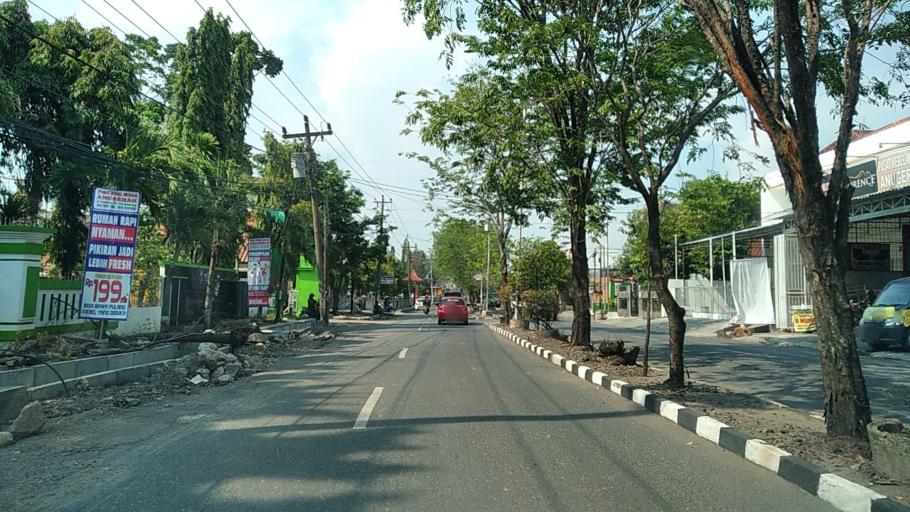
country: ID
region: Central Java
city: Semarang
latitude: -6.9965
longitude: 110.4566
